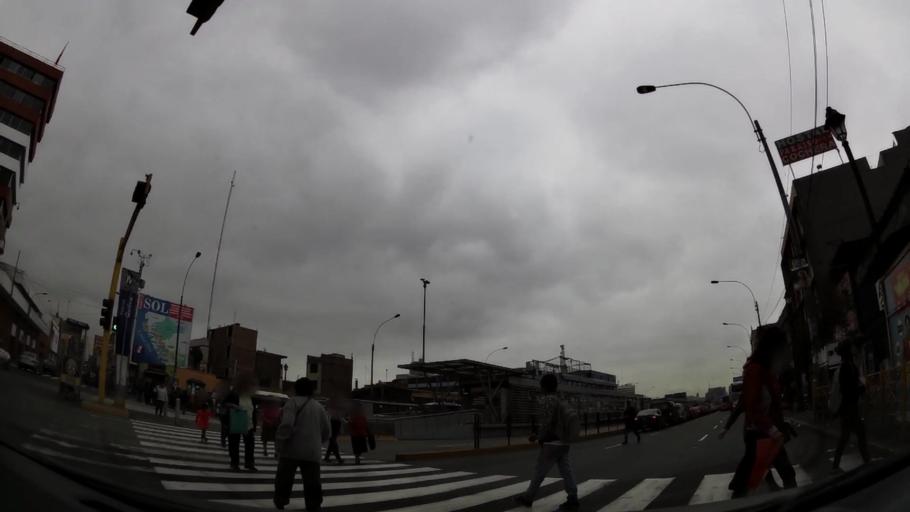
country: PE
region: Lima
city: Lima
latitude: -12.0509
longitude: -77.0426
